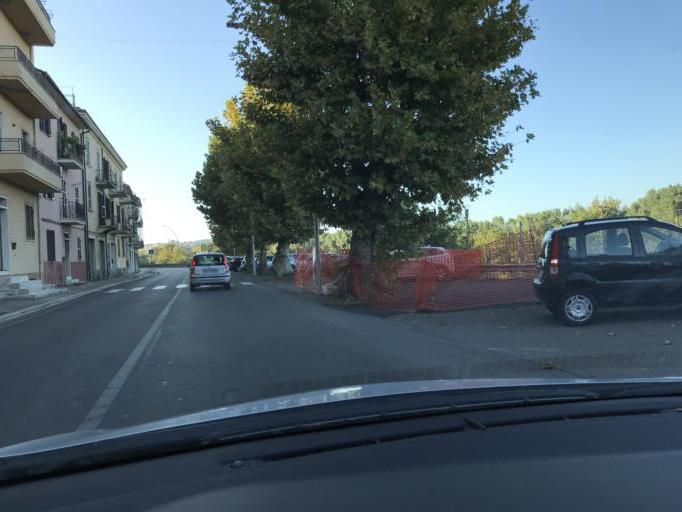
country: IT
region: Latium
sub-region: Provincia di Viterbo
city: Orte Scalo
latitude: 42.4418
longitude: 12.4068
